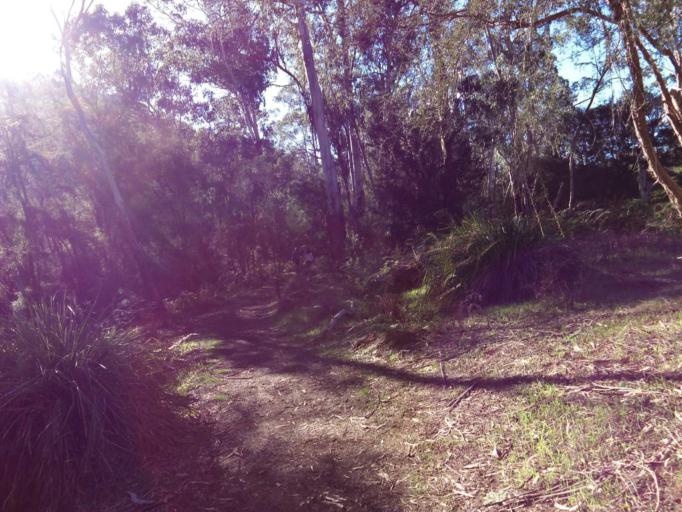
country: AU
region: Victoria
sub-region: Nillumbik
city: North Warrandyte
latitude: -37.7345
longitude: 145.1986
